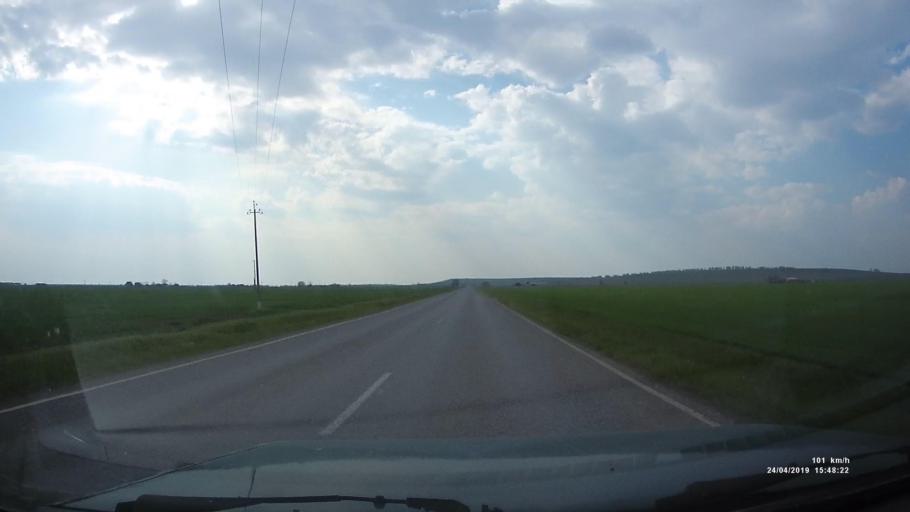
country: RU
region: Kalmykiya
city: Yashalta
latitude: 46.5982
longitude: 42.6775
